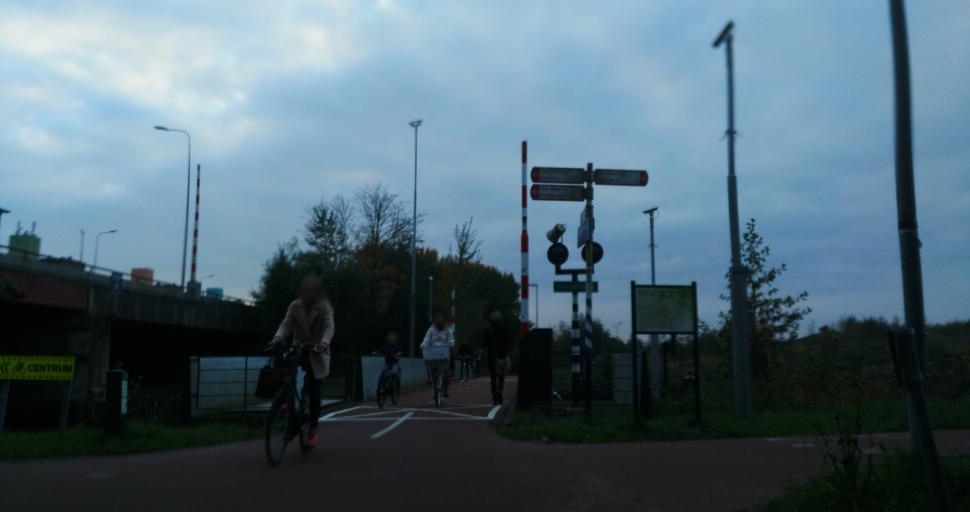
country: NL
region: Groningen
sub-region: Gemeente Groningen
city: Korrewegwijk
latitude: 53.2350
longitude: 6.5303
